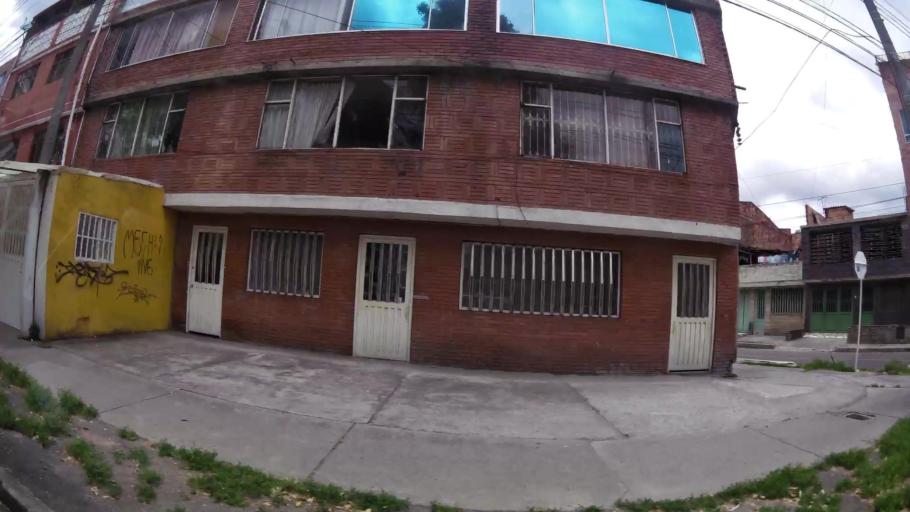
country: CO
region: Bogota D.C.
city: Bogota
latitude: 4.6158
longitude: -74.1164
